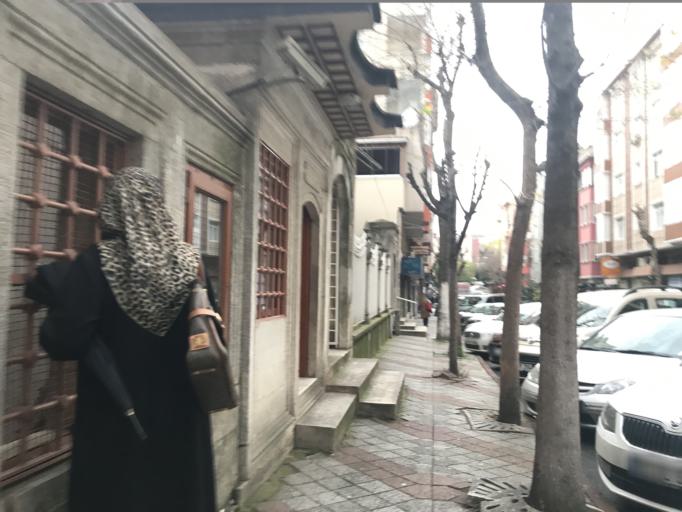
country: TR
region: Istanbul
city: Istanbul
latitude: 41.0201
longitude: 28.9448
